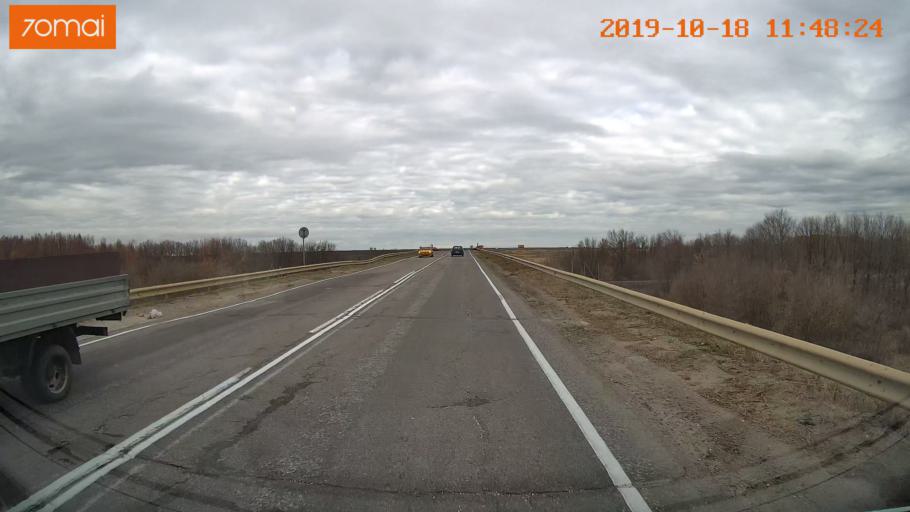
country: RU
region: Rjazan
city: Mikhaylov
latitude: 54.2391
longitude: 38.9825
